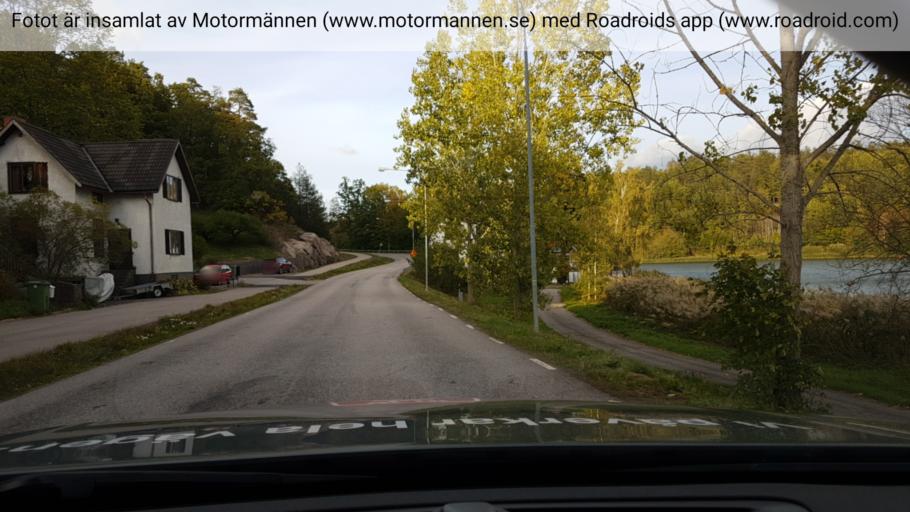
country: SE
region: Kalmar
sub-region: Vasterviks Kommun
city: Gamleby
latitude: 57.9018
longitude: 16.4125
